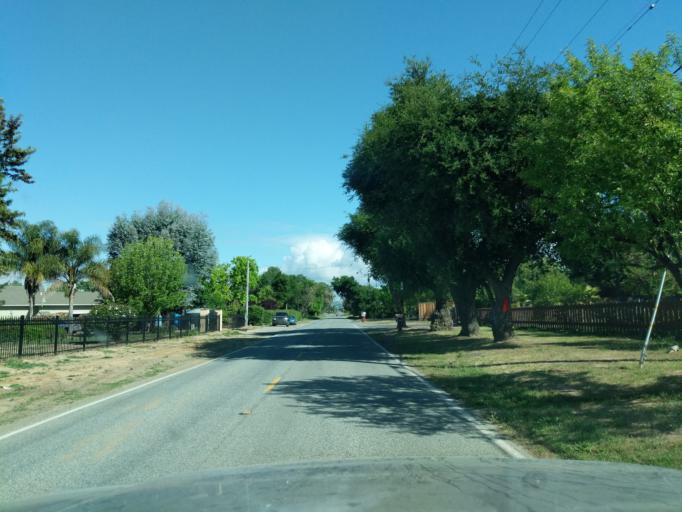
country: US
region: California
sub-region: Santa Clara County
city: San Martin
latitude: 37.0913
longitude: -121.5796
